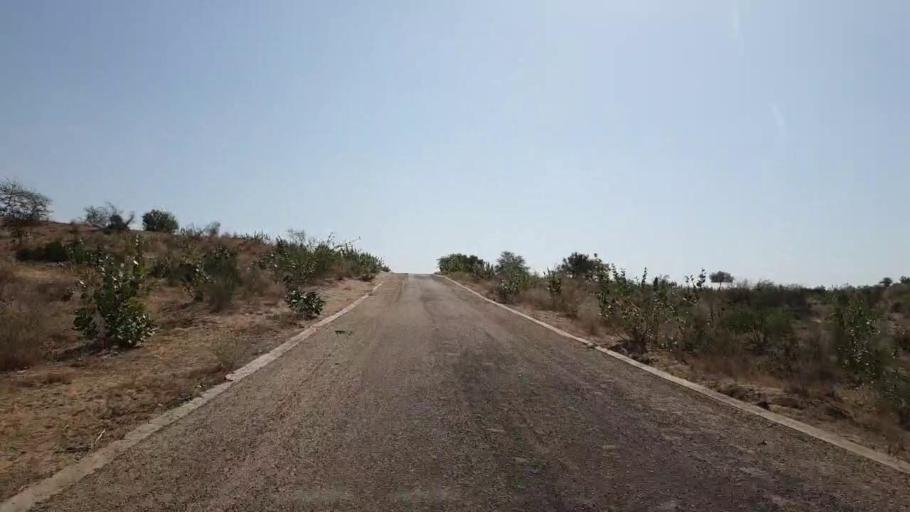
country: PK
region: Sindh
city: Umarkot
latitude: 25.1641
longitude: 70.0321
